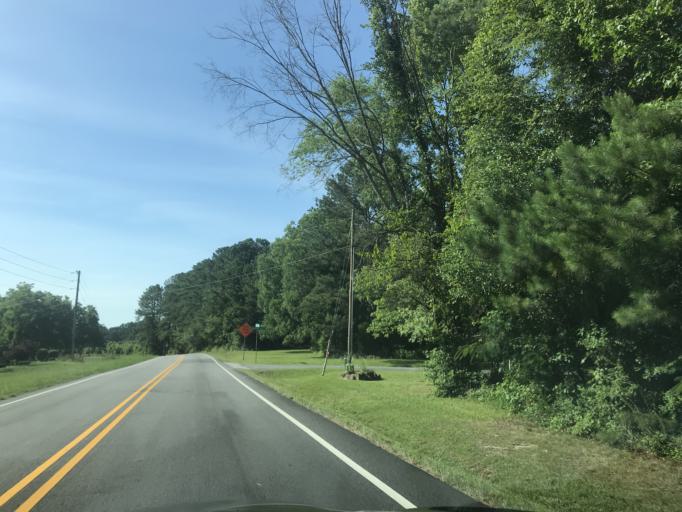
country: US
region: North Carolina
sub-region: Wake County
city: Garner
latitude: 35.6589
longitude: -78.5439
